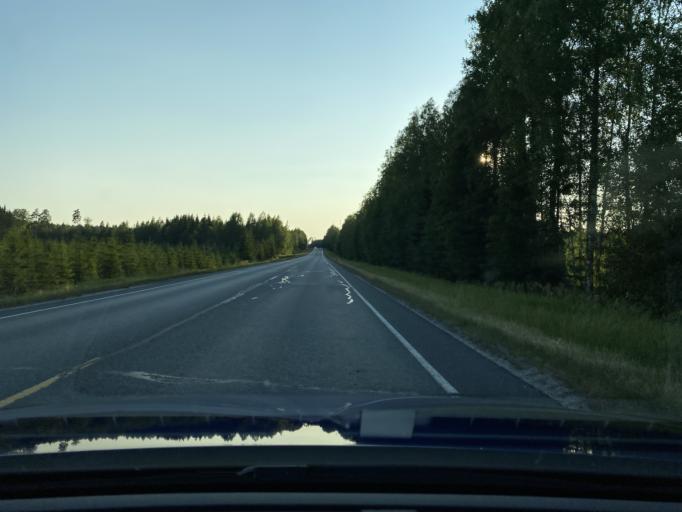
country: FI
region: Haeme
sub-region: Forssa
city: Tammela
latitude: 60.8279
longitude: 23.8931
